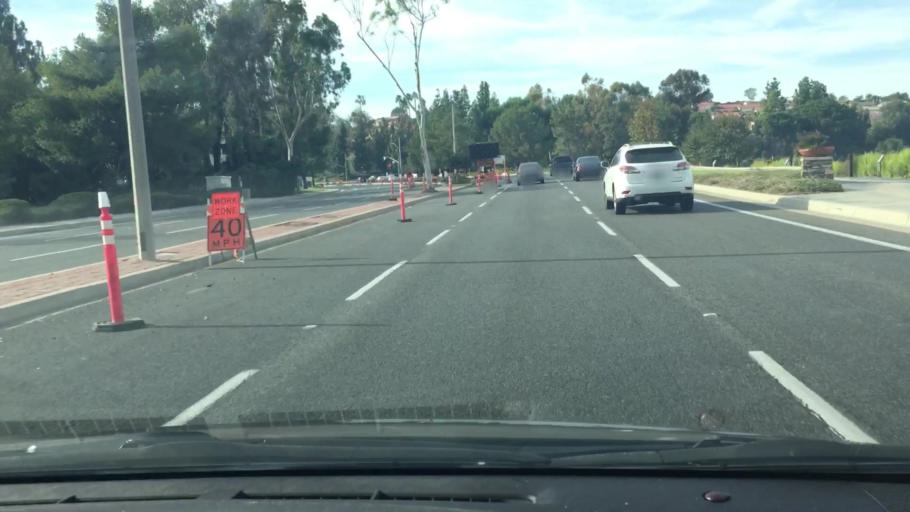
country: US
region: California
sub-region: Orange County
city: Mission Viejo
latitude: 33.6269
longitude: -117.6487
